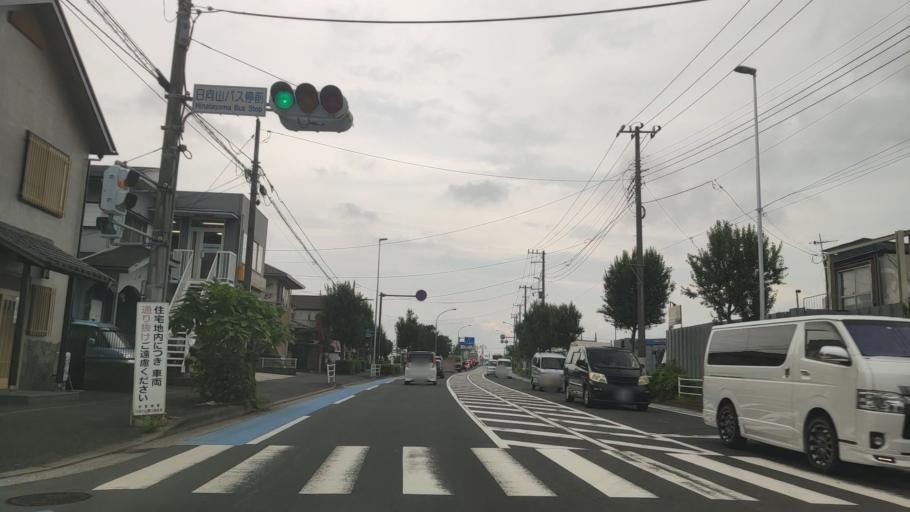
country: JP
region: Kanagawa
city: Minami-rinkan
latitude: 35.4411
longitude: 139.4845
